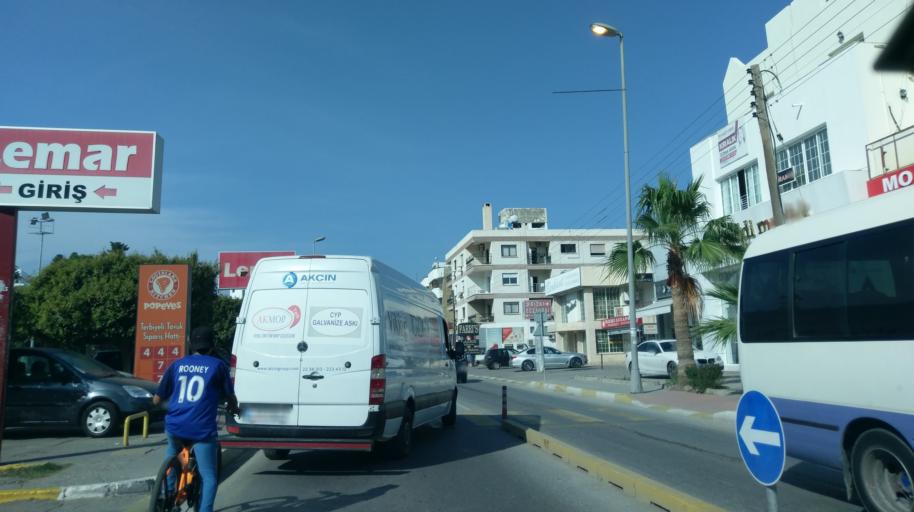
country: CY
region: Keryneia
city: Kyrenia
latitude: 35.3369
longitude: 33.3064
